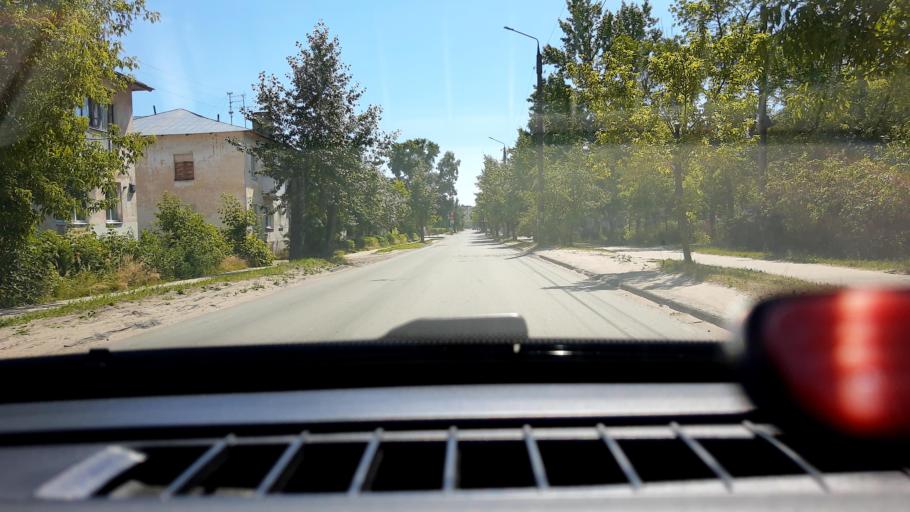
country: RU
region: Nizjnij Novgorod
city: Dzerzhinsk
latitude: 56.2491
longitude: 43.4730
